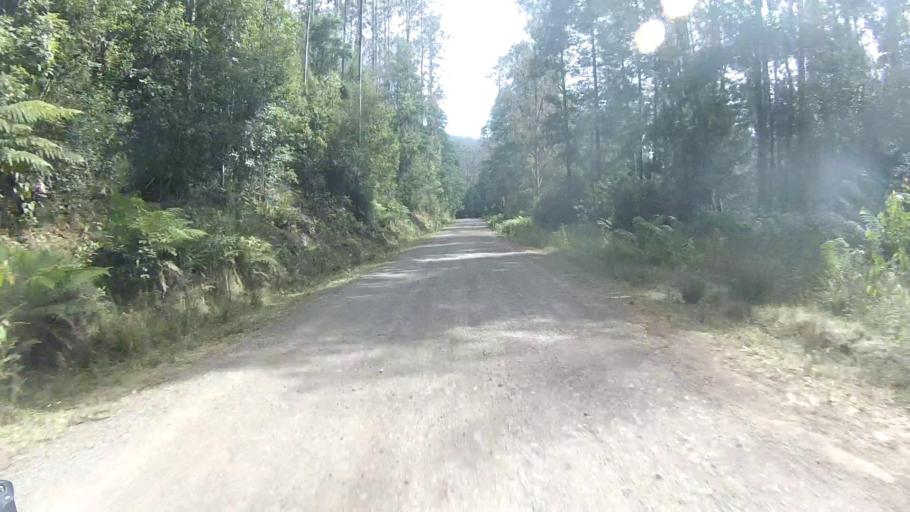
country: AU
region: Tasmania
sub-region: Sorell
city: Sorell
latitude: -42.7193
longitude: 147.8399
